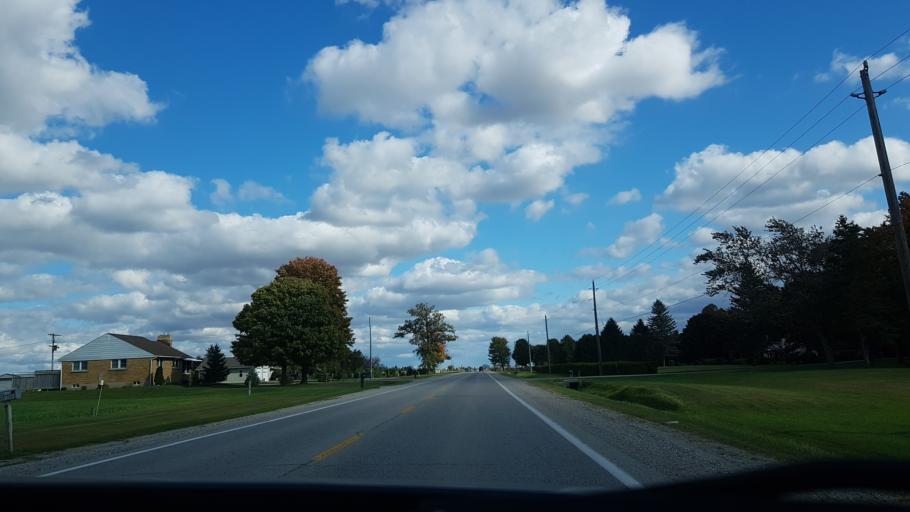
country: CA
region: Ontario
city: South Huron
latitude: 43.1510
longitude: -81.6731
